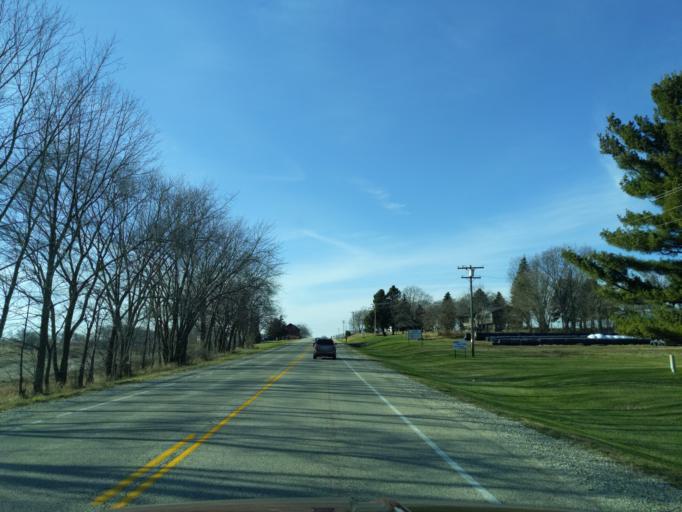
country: US
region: Wisconsin
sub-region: Jefferson County
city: Fort Atkinson
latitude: 42.8290
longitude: -88.8402
